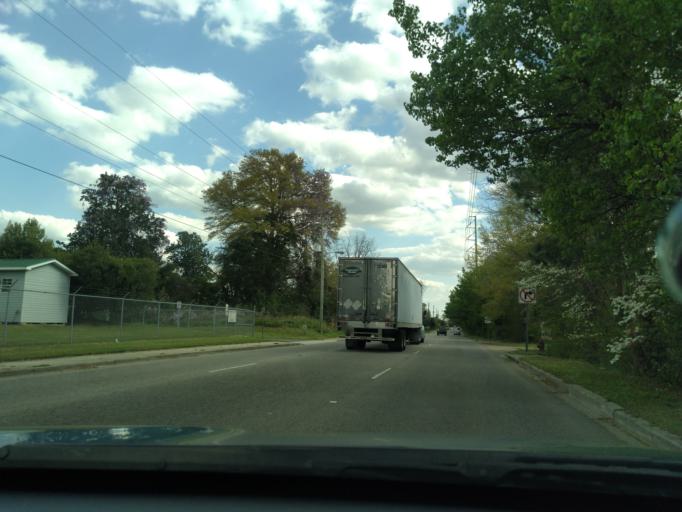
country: US
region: South Carolina
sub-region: Florence County
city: Florence
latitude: 34.1889
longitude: -79.7626
